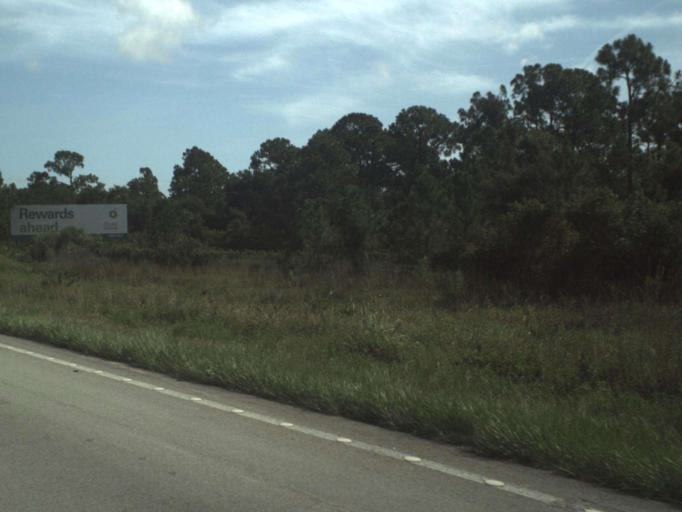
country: US
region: Florida
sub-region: Indian River County
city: West Vero Corridor
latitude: 27.6536
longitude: -80.5230
